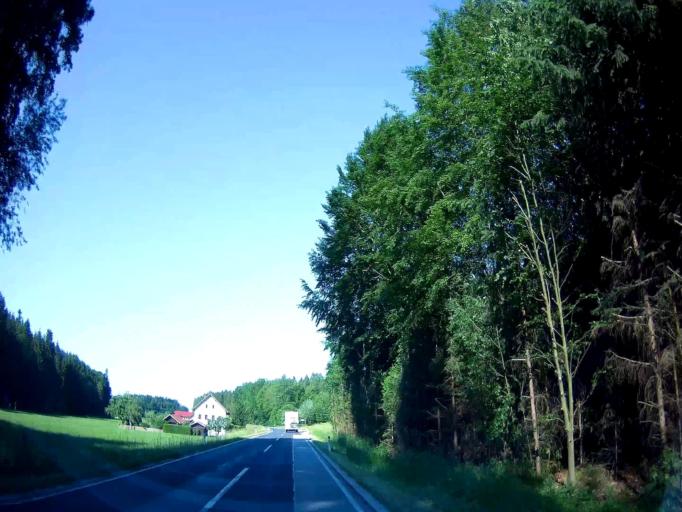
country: AT
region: Upper Austria
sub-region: Politischer Bezirk Braunau am Inn
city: Braunau am Inn
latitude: 48.1491
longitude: 13.0313
